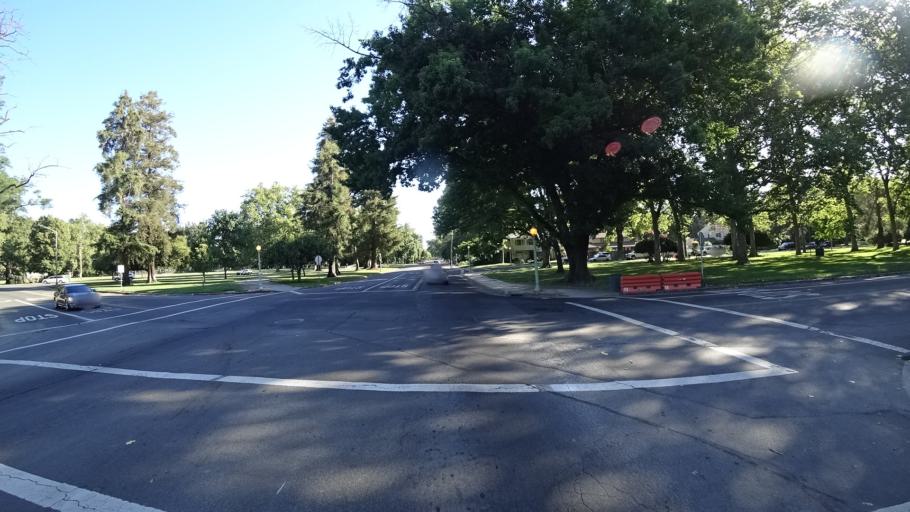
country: US
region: California
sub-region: Sacramento County
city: Sacramento
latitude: 38.5435
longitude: -121.5010
